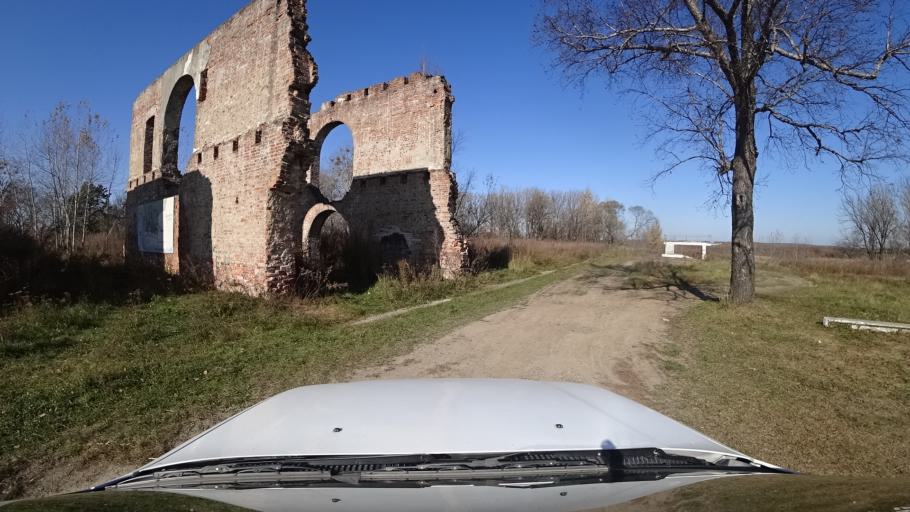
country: RU
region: Primorskiy
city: Dal'nerechensk
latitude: 45.9459
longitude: 133.6864
